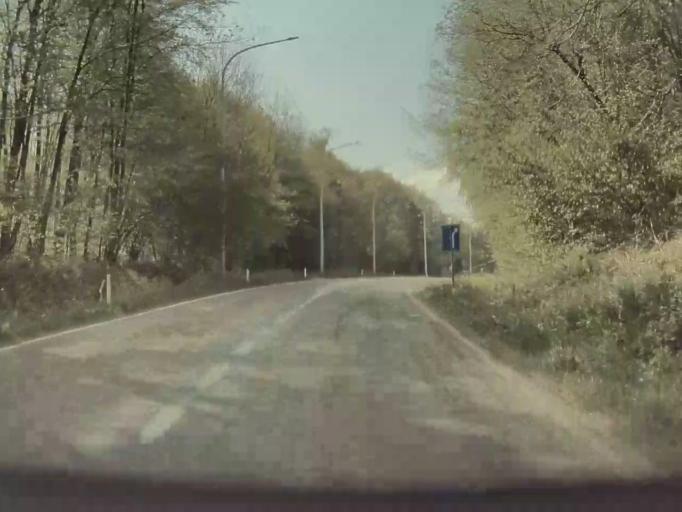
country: BE
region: Wallonia
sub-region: Province du Luxembourg
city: Tellin
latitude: 50.0553
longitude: 5.2101
